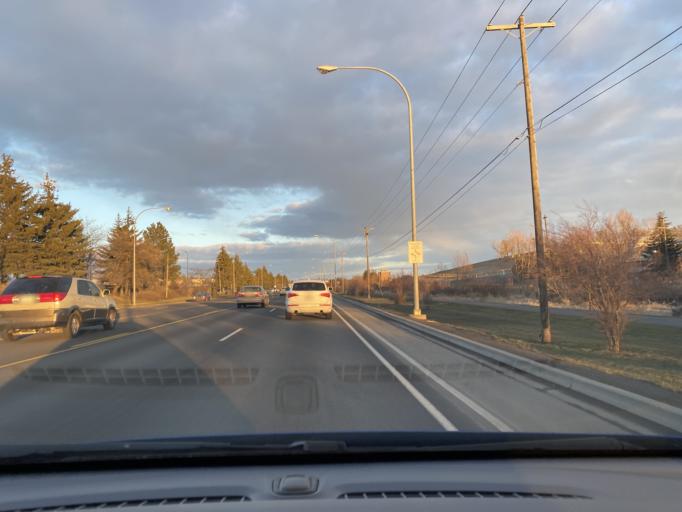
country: US
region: Idaho
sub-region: Latah County
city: Moscow
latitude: 46.7324
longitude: -117.0328
